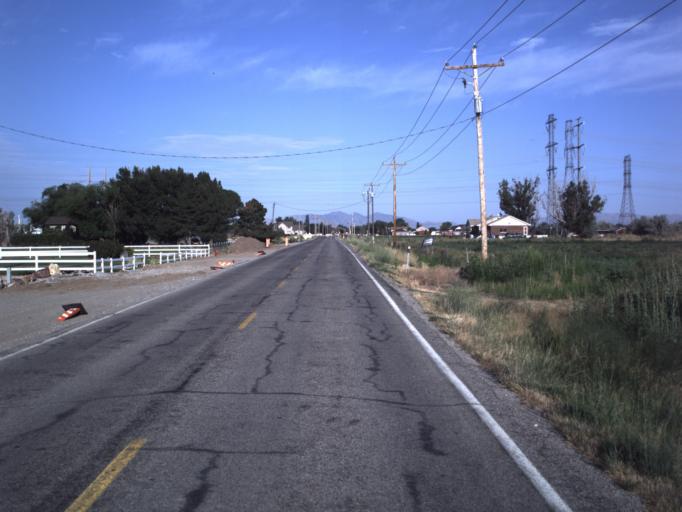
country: US
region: Utah
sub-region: Weber County
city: Farr West
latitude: 41.3050
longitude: -112.0525
